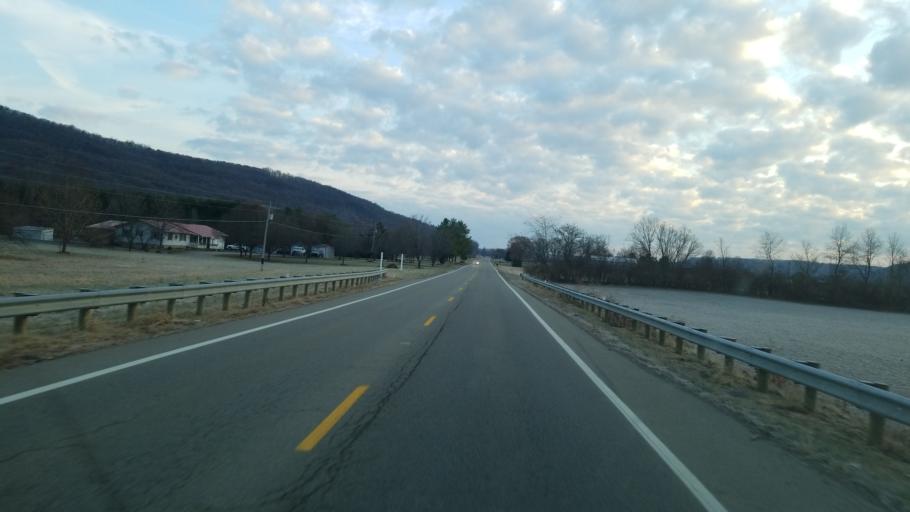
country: US
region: Ohio
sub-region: Ross County
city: Frankfort
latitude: 39.2400
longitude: -83.2284
